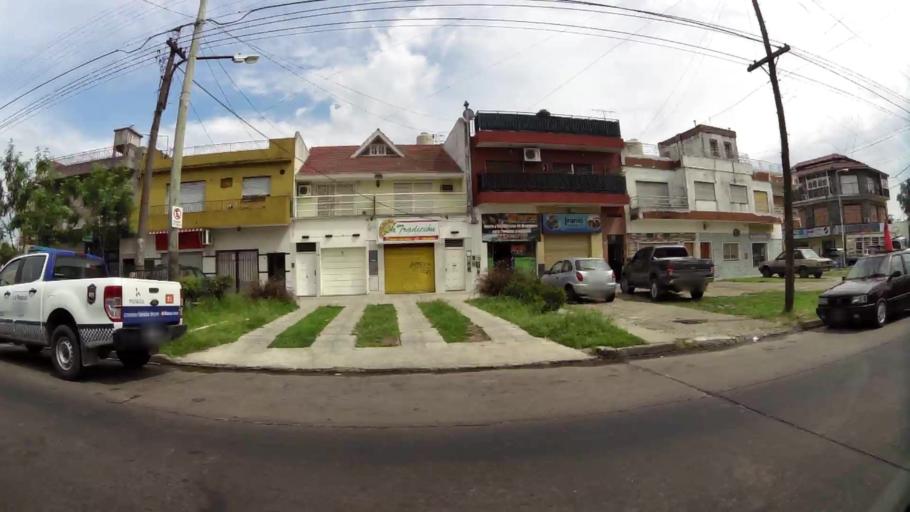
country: AR
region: Buenos Aires F.D.
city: Villa Lugano
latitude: -34.6950
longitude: -58.5034
